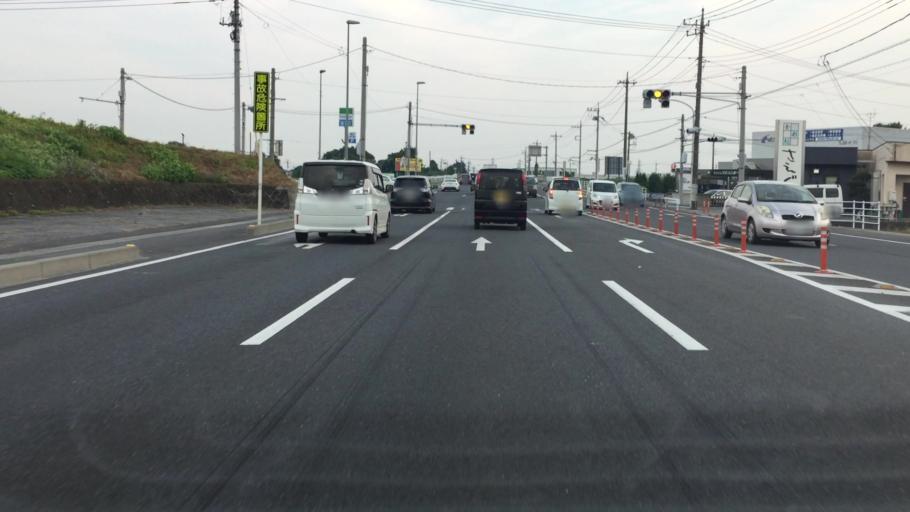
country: JP
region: Tochigi
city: Tochigi
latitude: 36.3564
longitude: 139.7142
